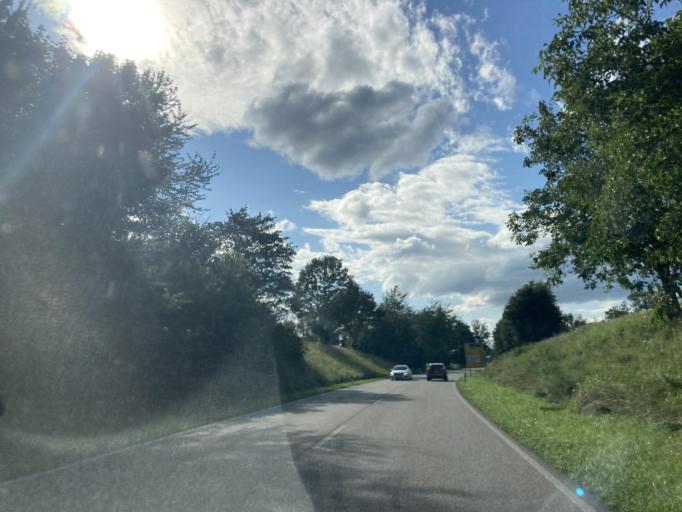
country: DE
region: Baden-Wuerttemberg
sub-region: Freiburg Region
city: Unterkrozingen
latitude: 47.9268
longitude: 7.6944
